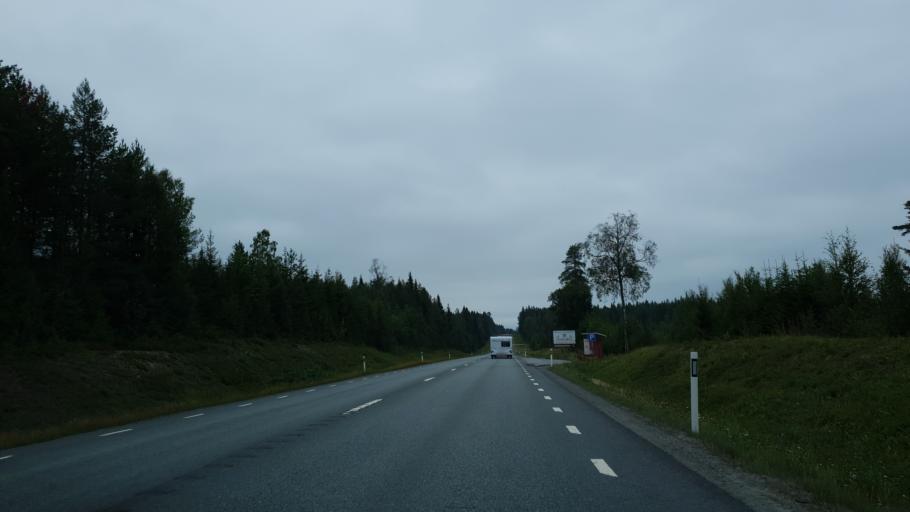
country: SE
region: Vaesterbotten
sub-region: Skelleftea Kommun
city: Burea
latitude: 64.3528
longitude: 21.2939
